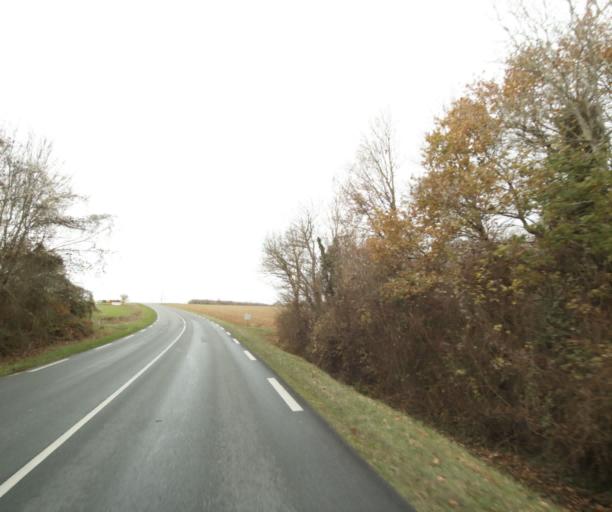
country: FR
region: Poitou-Charentes
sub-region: Departement de la Charente-Maritime
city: Corme-Royal
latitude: 45.7369
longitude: -0.7813
